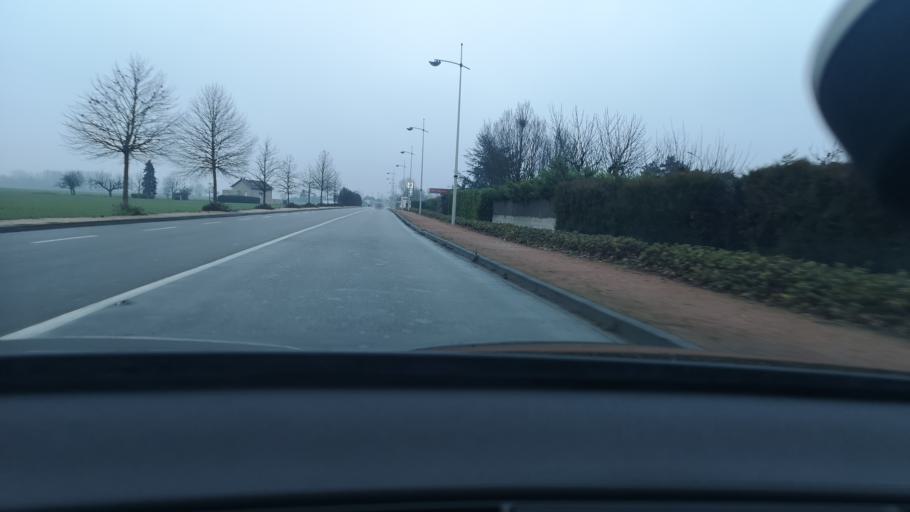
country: FR
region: Bourgogne
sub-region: Departement de la Cote-d'Or
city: Longvic
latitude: 47.2823
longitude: 5.0629
